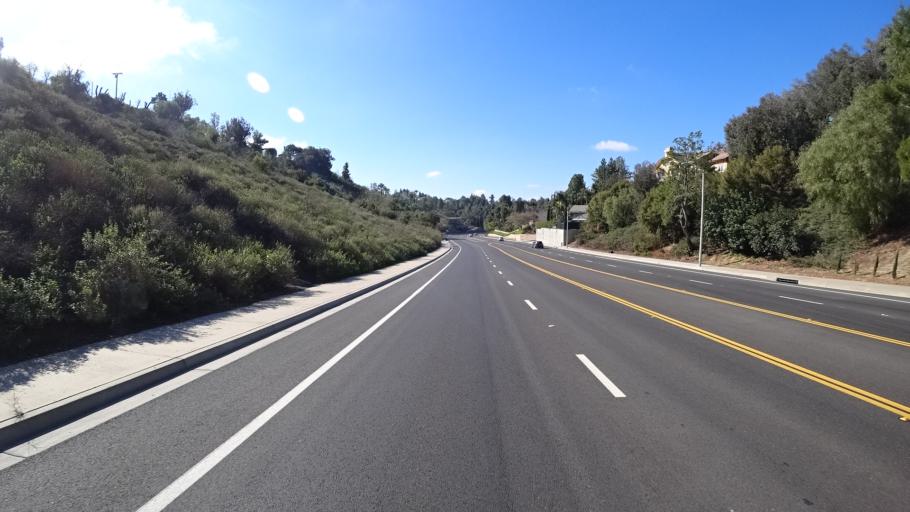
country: US
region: California
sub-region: Orange County
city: North Tustin
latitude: 33.7769
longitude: -117.7781
